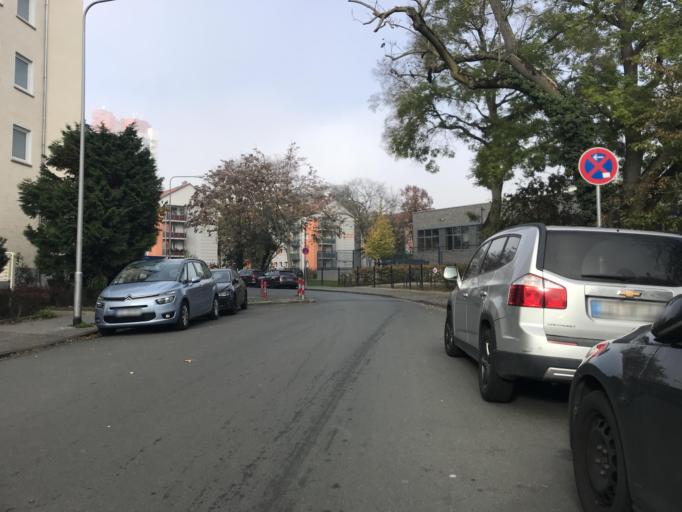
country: DE
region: Hesse
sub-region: Regierungsbezirk Darmstadt
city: Wiesbaden
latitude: 50.0419
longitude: 8.2446
